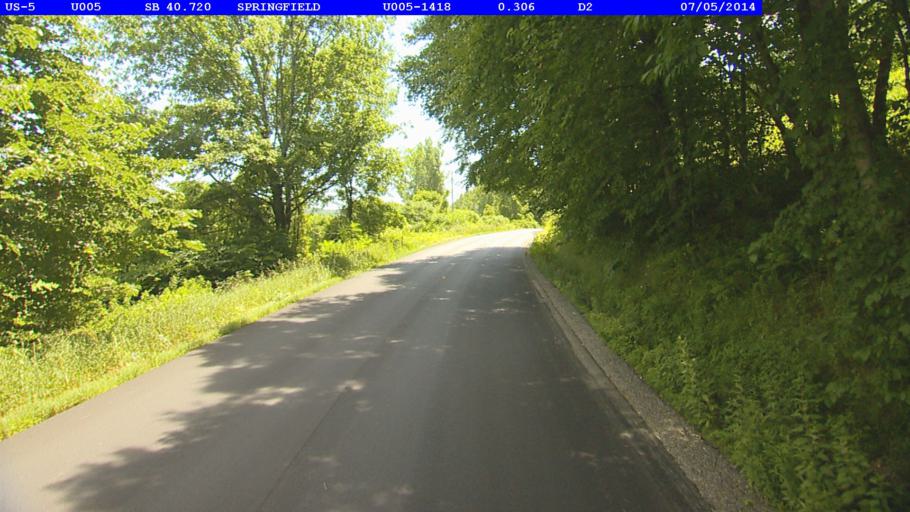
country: US
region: New Hampshire
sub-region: Sullivan County
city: Charlestown
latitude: 43.2376
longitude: -72.4383
